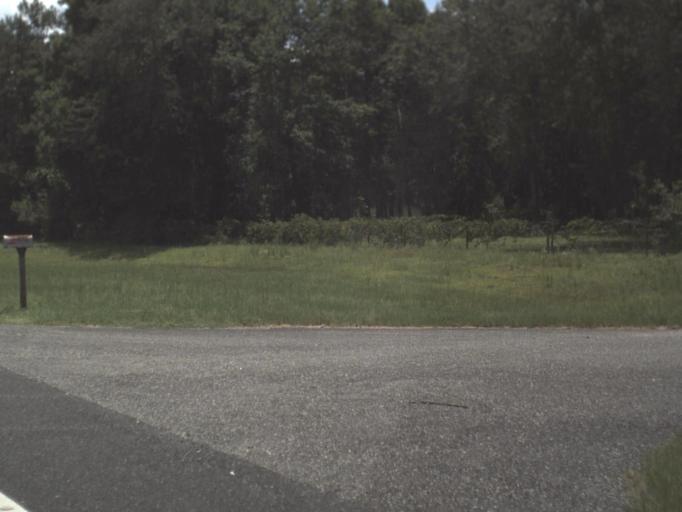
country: US
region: Florida
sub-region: Levy County
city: Williston
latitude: 29.3618
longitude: -82.4062
